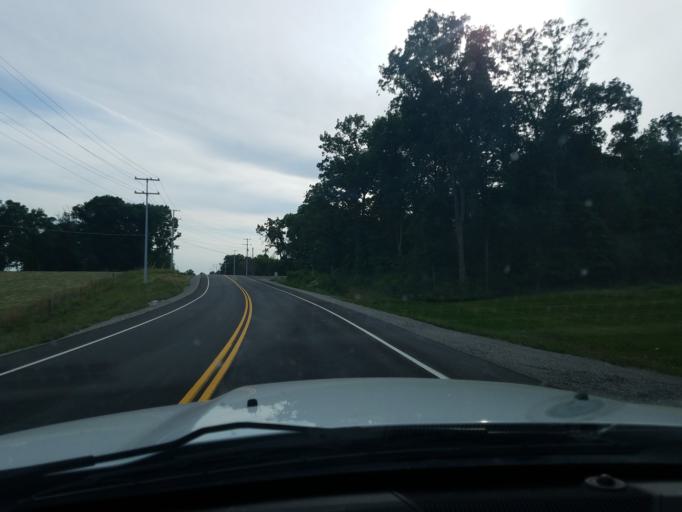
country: US
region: Tennessee
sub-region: Putnam County
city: Baxter
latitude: 36.1370
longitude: -85.5858
